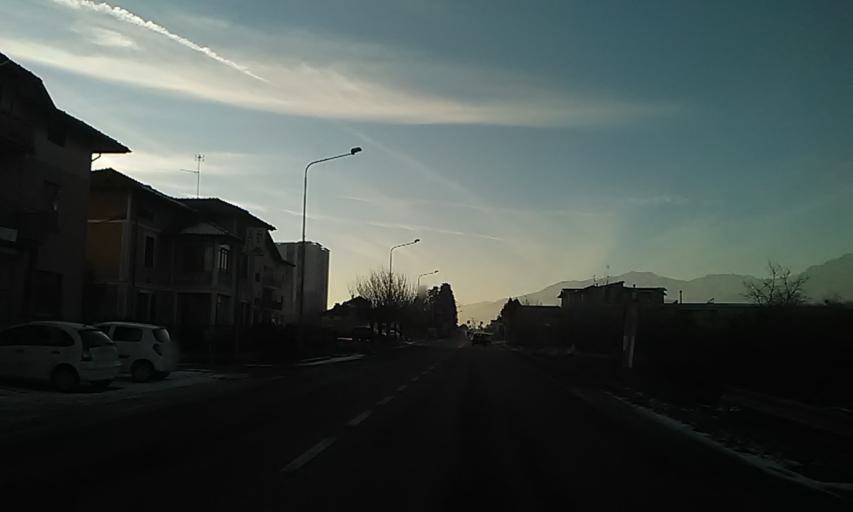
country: IT
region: Piedmont
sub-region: Provincia di Biella
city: Valdengo
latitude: 45.5637
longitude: 8.1443
